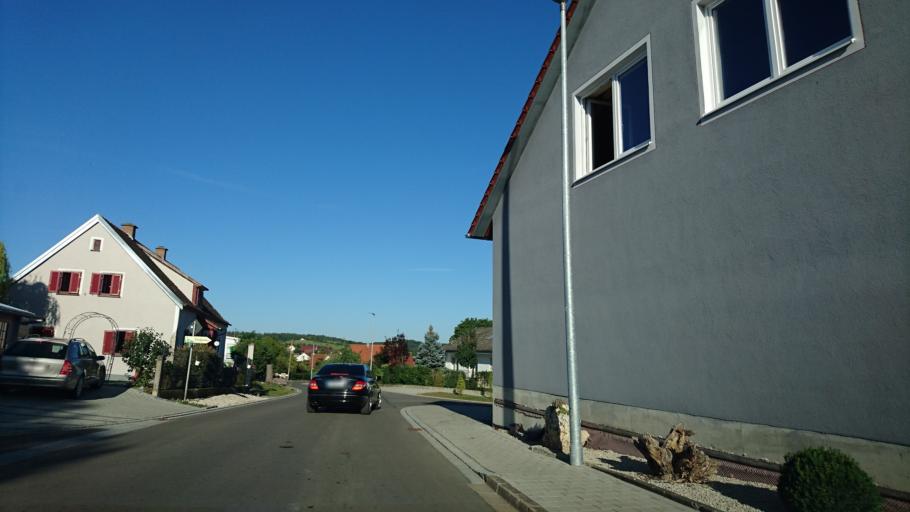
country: DE
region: Bavaria
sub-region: Swabia
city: Funfstetten
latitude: 48.8314
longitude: 10.7698
